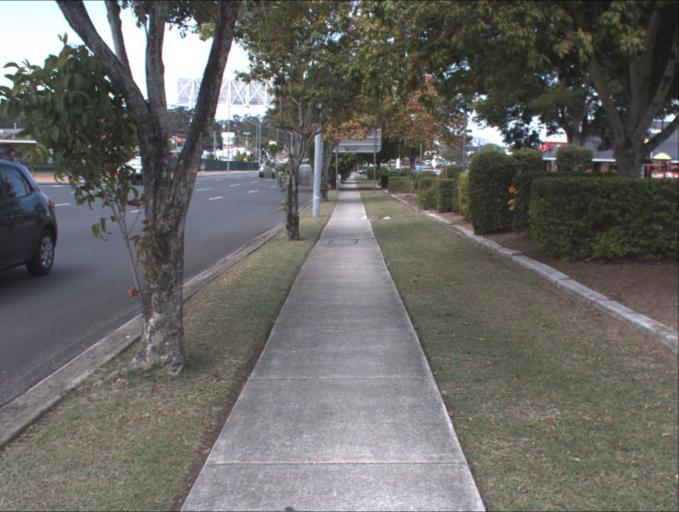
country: AU
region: Queensland
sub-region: Brisbane
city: Sunnybank Hills
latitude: -27.6606
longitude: 153.0385
